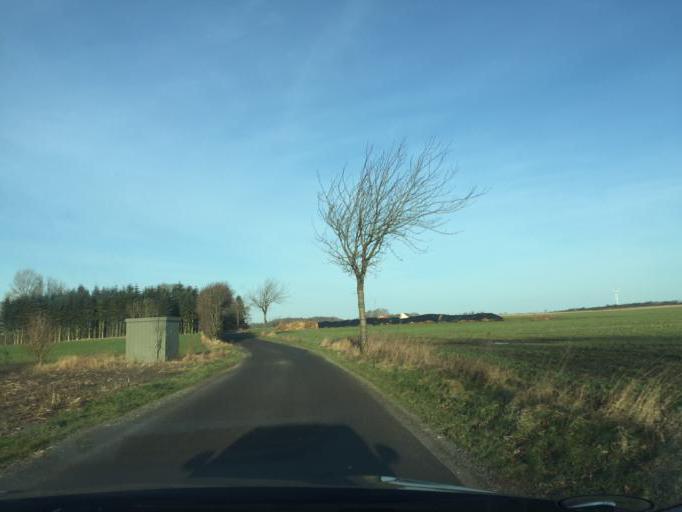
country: DK
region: South Denmark
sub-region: Middelfart Kommune
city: Ejby
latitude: 55.4496
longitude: 9.9307
